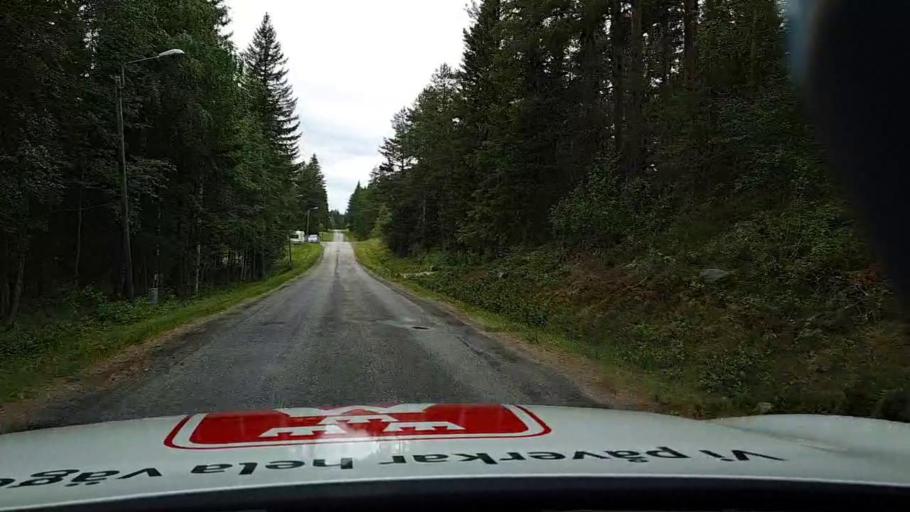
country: SE
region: Vaesterbotten
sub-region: Dorotea Kommun
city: Dorotea
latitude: 64.0993
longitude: 16.4086
